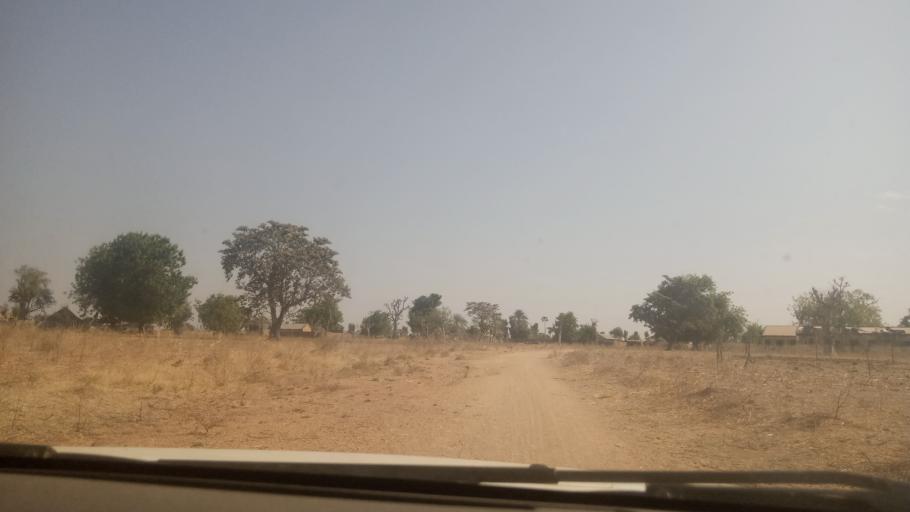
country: NG
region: Adamawa
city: Mayo Belwa
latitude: 9.0812
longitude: 12.0350
